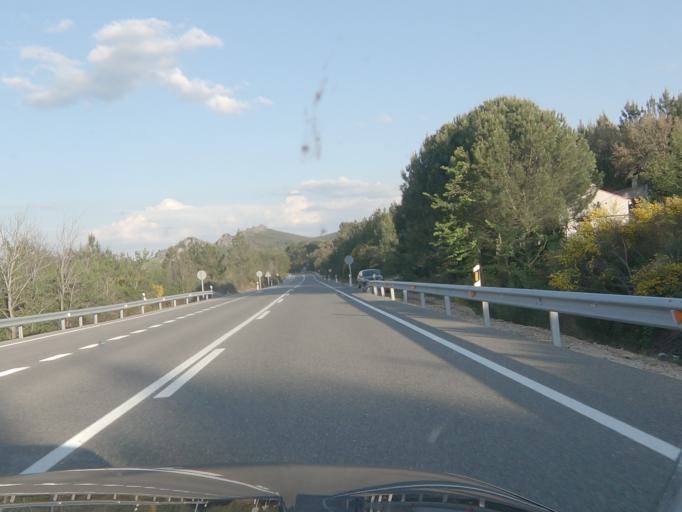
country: PT
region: Portalegre
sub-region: Portalegre
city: Sao Juliao
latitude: 39.3454
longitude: -7.2976
